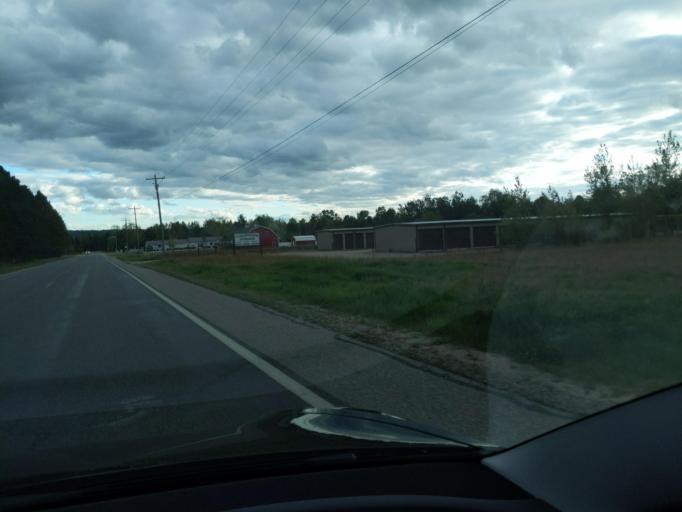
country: US
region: Michigan
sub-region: Kalkaska County
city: Rapid City
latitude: 44.8155
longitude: -85.2828
